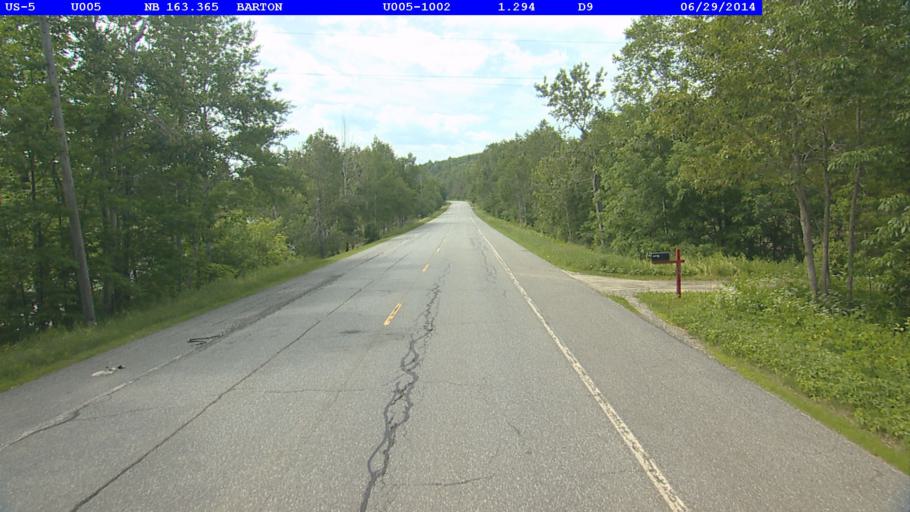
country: US
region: Vermont
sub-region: Caledonia County
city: Lyndonville
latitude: 44.7084
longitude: -72.1184
